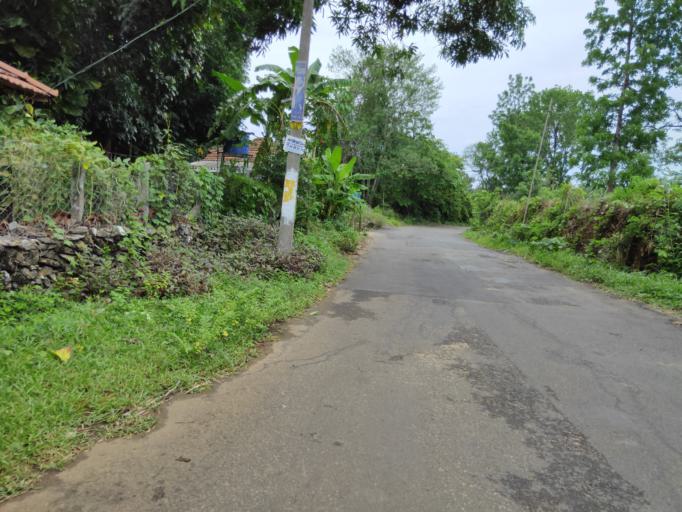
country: IN
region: Kerala
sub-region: Malappuram
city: Manjeri
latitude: 11.2357
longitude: 76.2484
